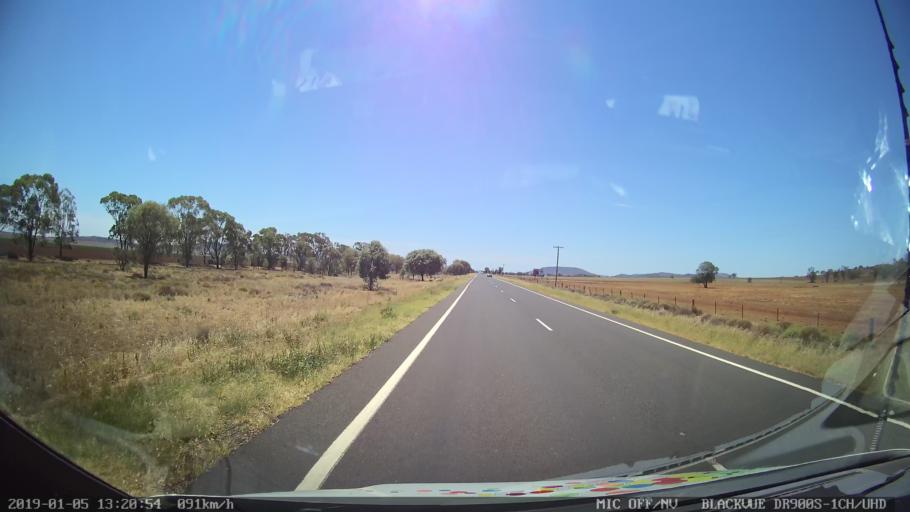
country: AU
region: New South Wales
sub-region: Gunnedah
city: Gunnedah
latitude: -31.0987
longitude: 149.9418
